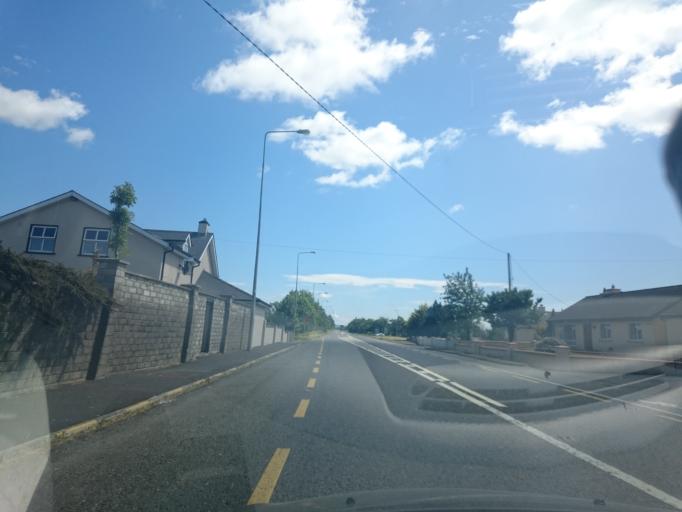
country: IE
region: Leinster
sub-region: Kilkenny
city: Thomastown
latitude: 52.6471
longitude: -7.1288
